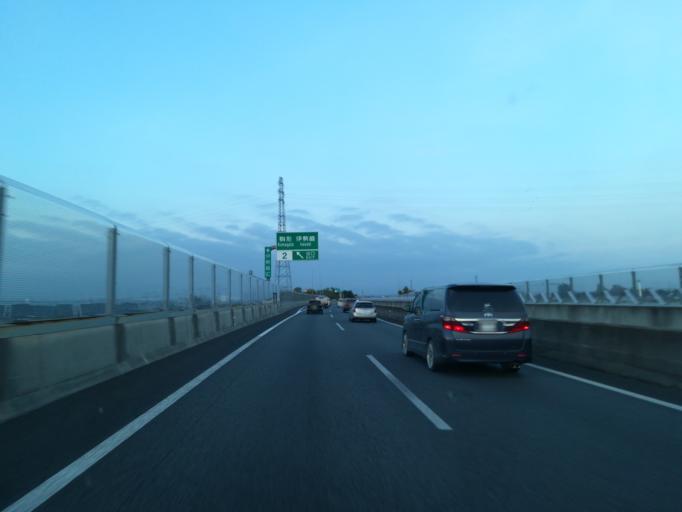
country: JP
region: Gunma
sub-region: Sawa-gun
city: Tamamura
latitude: 36.3450
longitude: 139.1399
